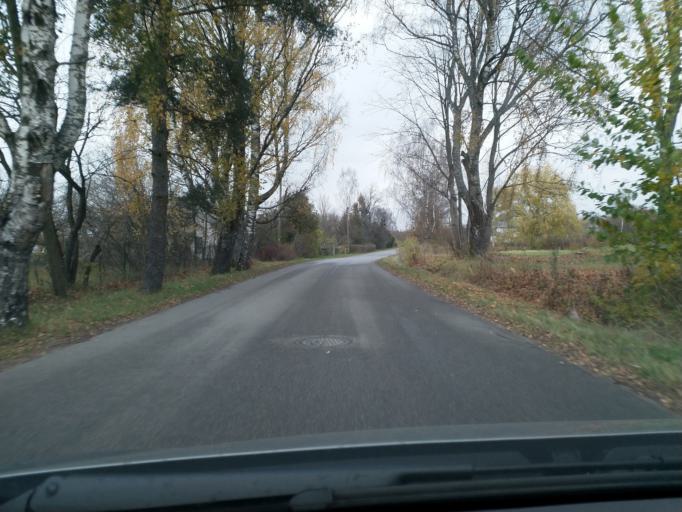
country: LV
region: Kuldigas Rajons
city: Kuldiga
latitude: 56.9744
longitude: 21.9777
